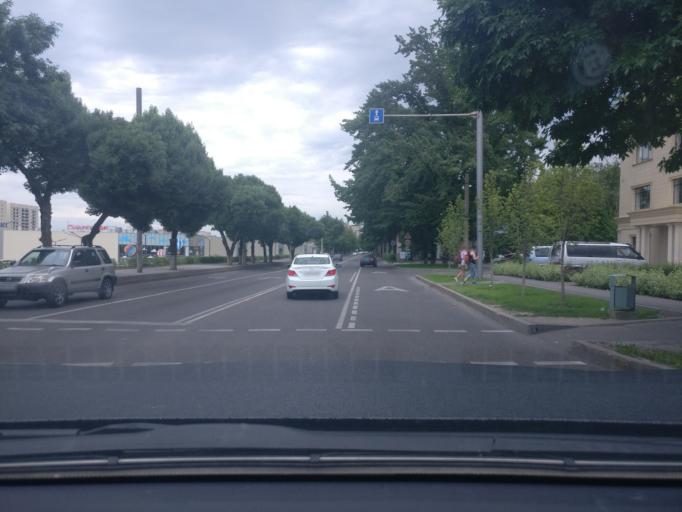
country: KZ
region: Almaty Qalasy
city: Almaty
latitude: 43.2369
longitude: 76.8527
